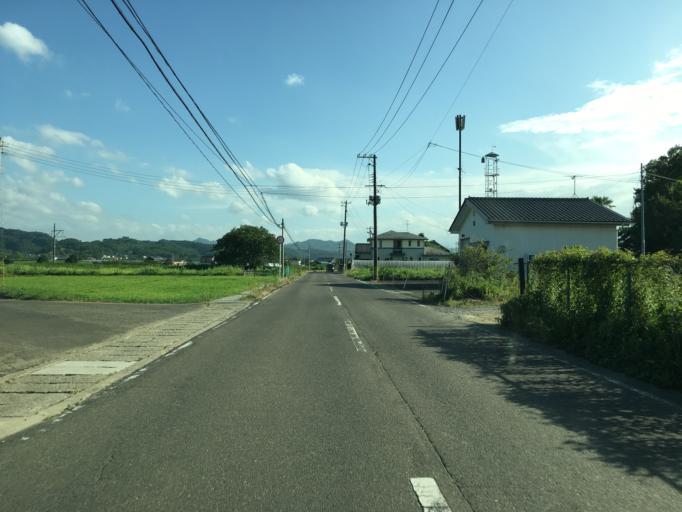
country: JP
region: Fukushima
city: Yanagawamachi-saiwaicho
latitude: 37.8314
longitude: 140.5832
